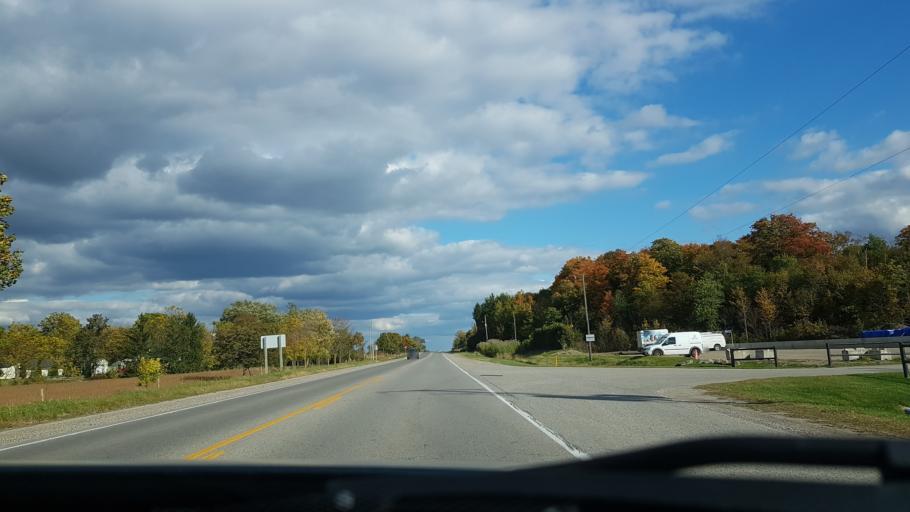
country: CA
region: Ontario
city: Delaware
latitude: 43.0001
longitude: -81.4183
